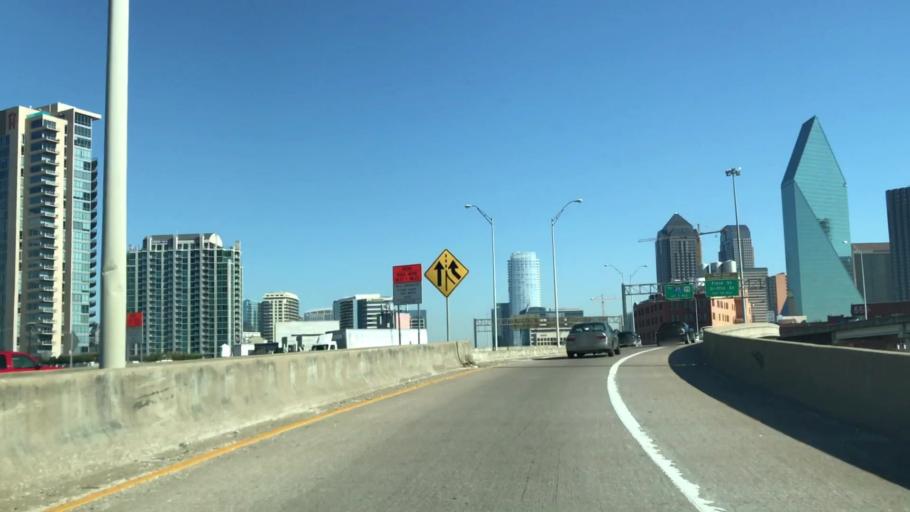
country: US
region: Texas
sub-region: Dallas County
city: Dallas
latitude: 32.7821
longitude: -96.8108
